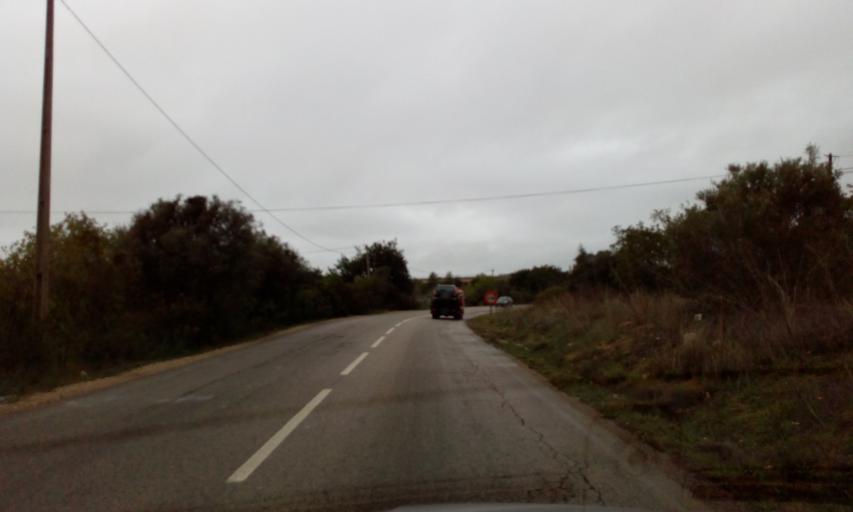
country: PT
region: Faro
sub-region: Albufeira
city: Ferreiras
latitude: 37.1377
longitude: -8.2664
